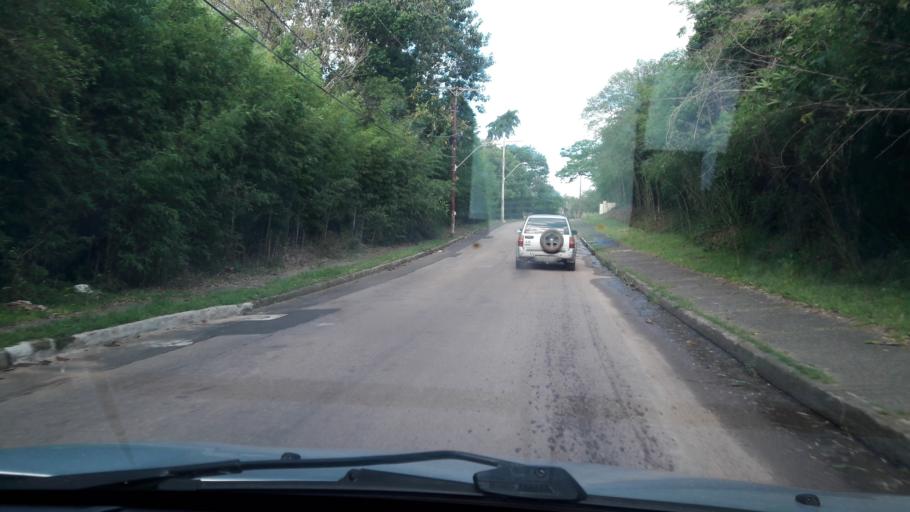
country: BR
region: Rio Grande do Sul
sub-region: Porto Alegre
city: Porto Alegre
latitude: -30.0846
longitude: -51.2047
